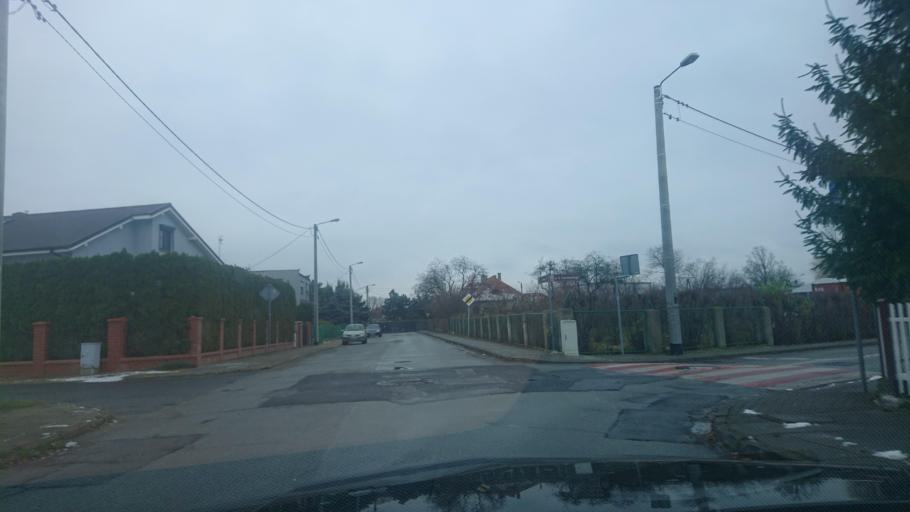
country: PL
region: Greater Poland Voivodeship
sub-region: Powiat gnieznienski
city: Gniezno
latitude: 52.5385
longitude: 17.5791
